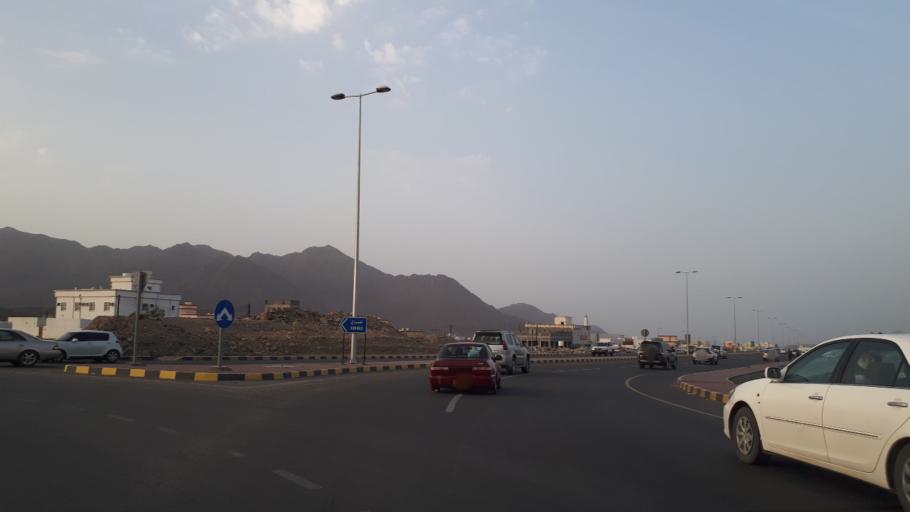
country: OM
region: Al Batinah
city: Rustaq
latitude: 23.4342
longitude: 57.3898
